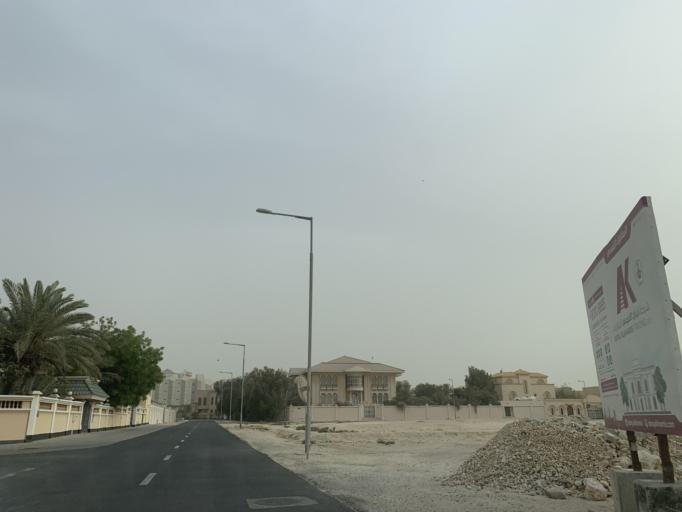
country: BH
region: Central Governorate
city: Madinat Hamad
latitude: 26.1397
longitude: 50.5245
